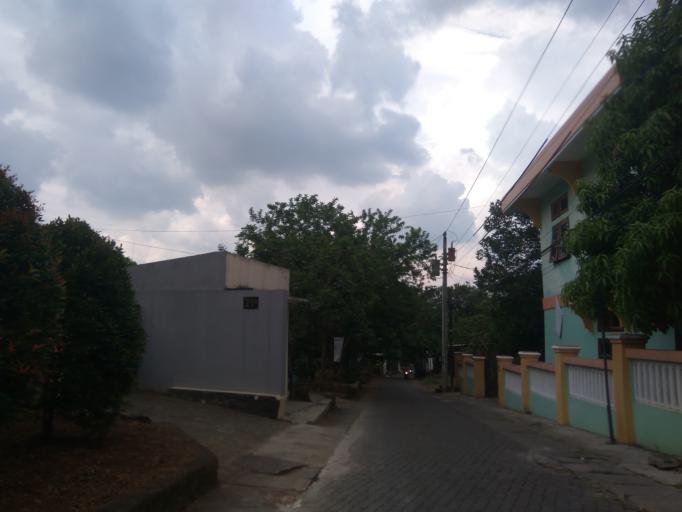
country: ID
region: Central Java
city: Semarang
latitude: -7.0643
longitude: 110.4420
